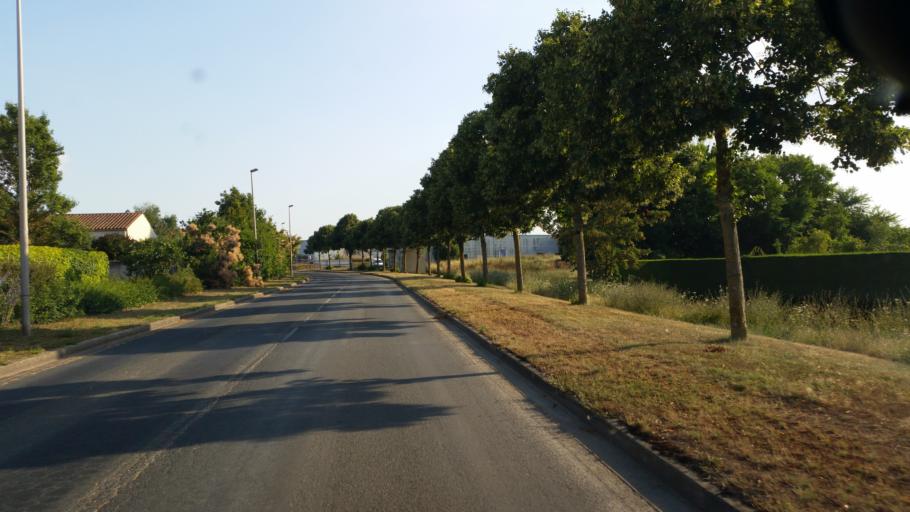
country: FR
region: Poitou-Charentes
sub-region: Departement de la Charente-Maritime
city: Marans
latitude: 46.3091
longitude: -1.0058
